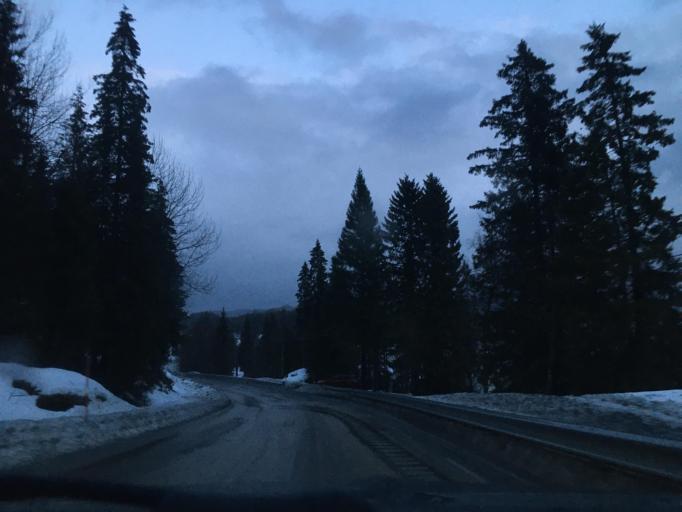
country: NO
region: Nordland
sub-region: Rana
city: Hauknes
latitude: 66.2993
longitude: 13.9284
